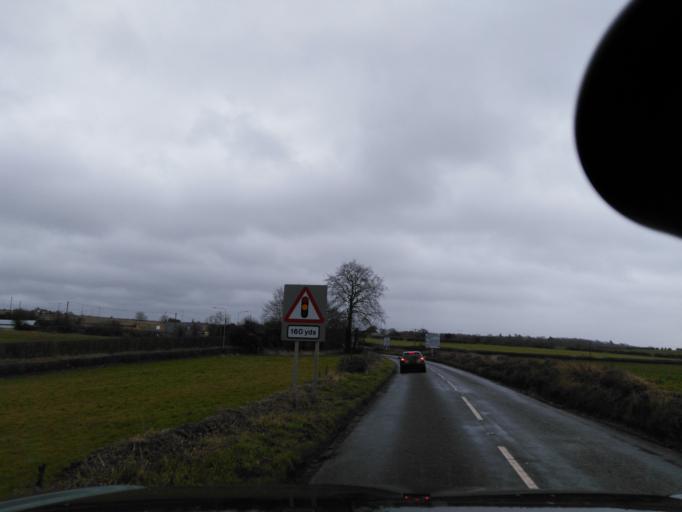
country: GB
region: England
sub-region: Wiltshire
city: Box
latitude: 51.4026
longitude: -2.2355
